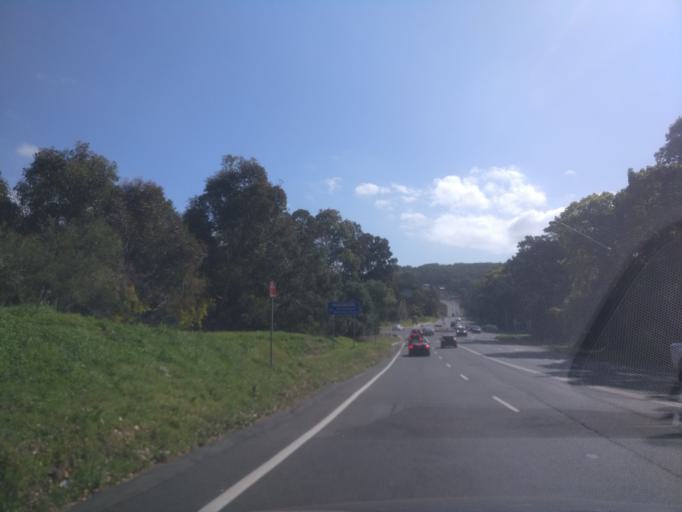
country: AU
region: New South Wales
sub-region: Pittwater
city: Warriewood
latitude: -33.6763
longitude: 151.2911
